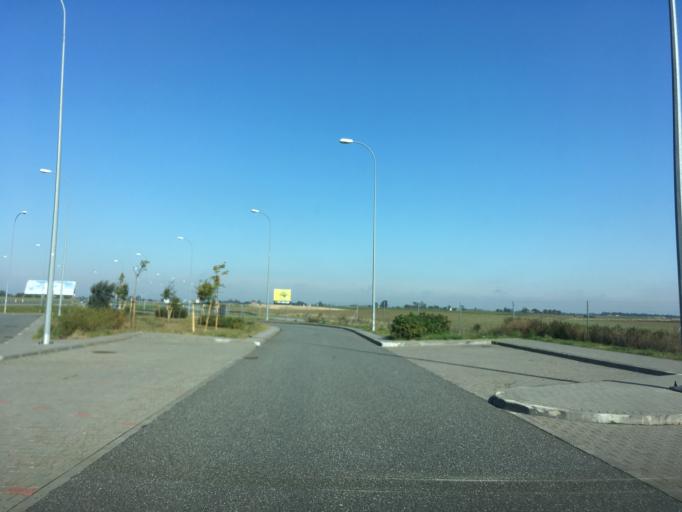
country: PL
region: Kujawsko-Pomorskie
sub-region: Powiat chelminski
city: Lisewo
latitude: 53.2594
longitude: 18.7252
